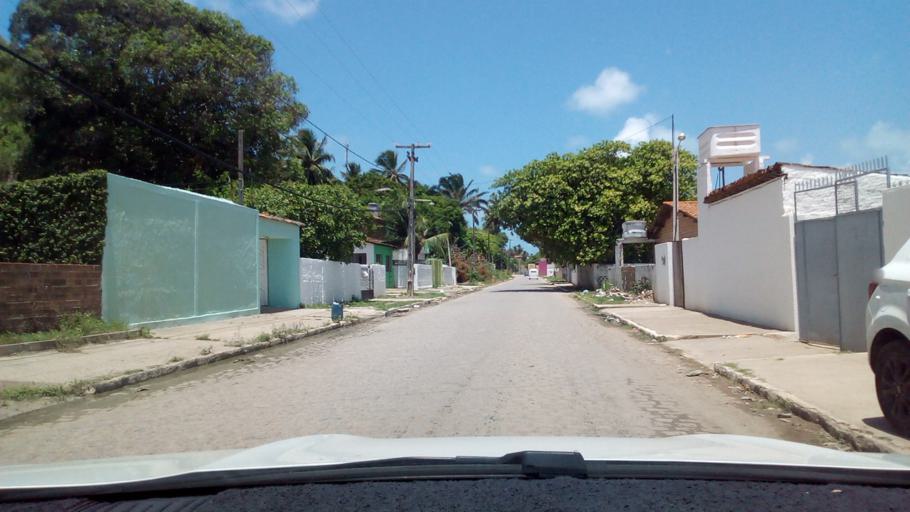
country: BR
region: Paraiba
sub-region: Pitimbu
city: Pitimbu
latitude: -7.4851
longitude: -34.8152
